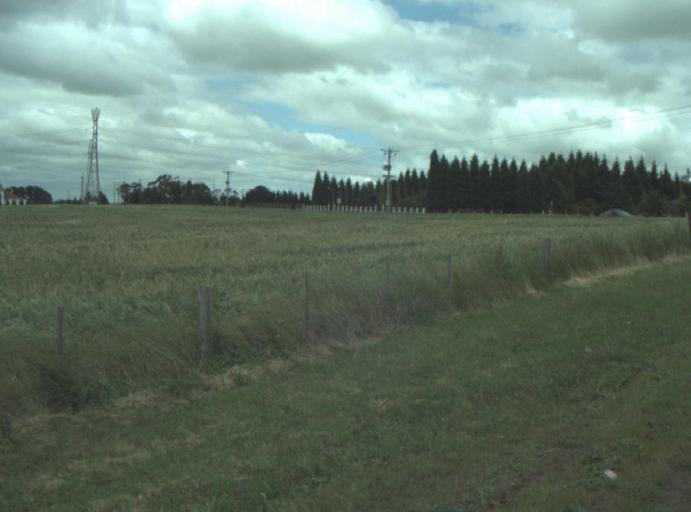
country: AU
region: Victoria
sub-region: Greater Geelong
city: Bell Post Hill
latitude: -38.0763
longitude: 144.3283
